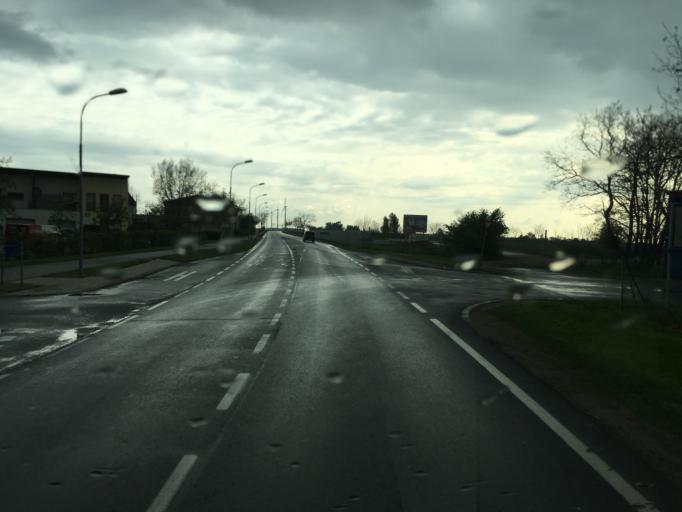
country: AT
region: Burgenland
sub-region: Politischer Bezirk Neusiedl am See
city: Parndorf
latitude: 48.0006
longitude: 16.8739
